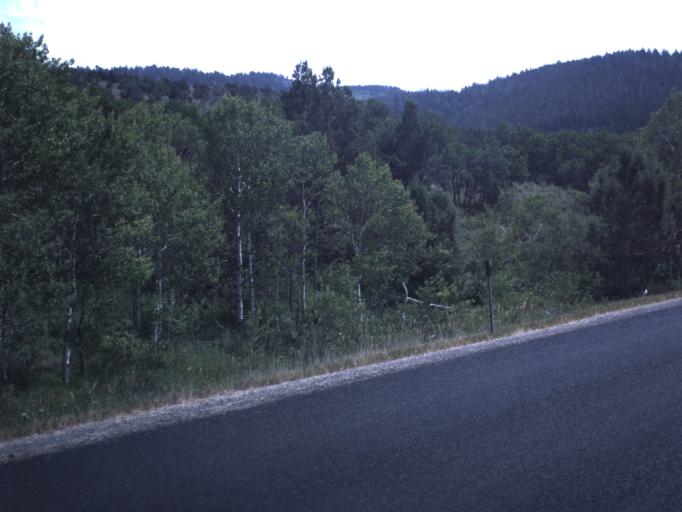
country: US
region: Utah
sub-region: Summit County
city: Francis
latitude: 40.5568
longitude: -111.1130
